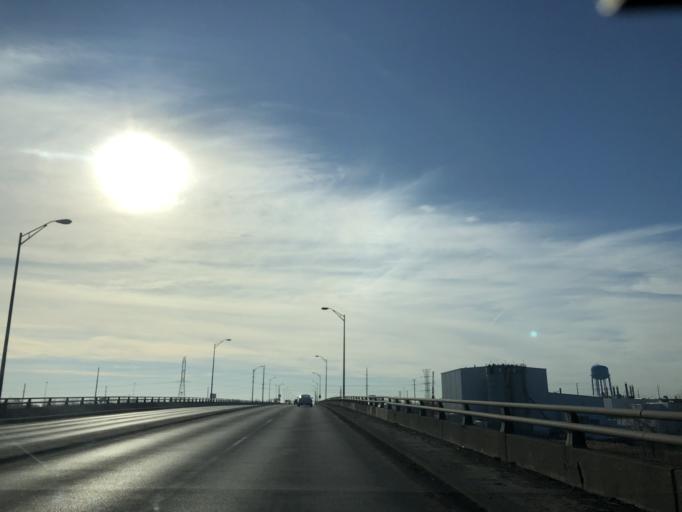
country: US
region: Illinois
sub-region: Cook County
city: Stickney
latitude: 41.8194
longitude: -87.7631
